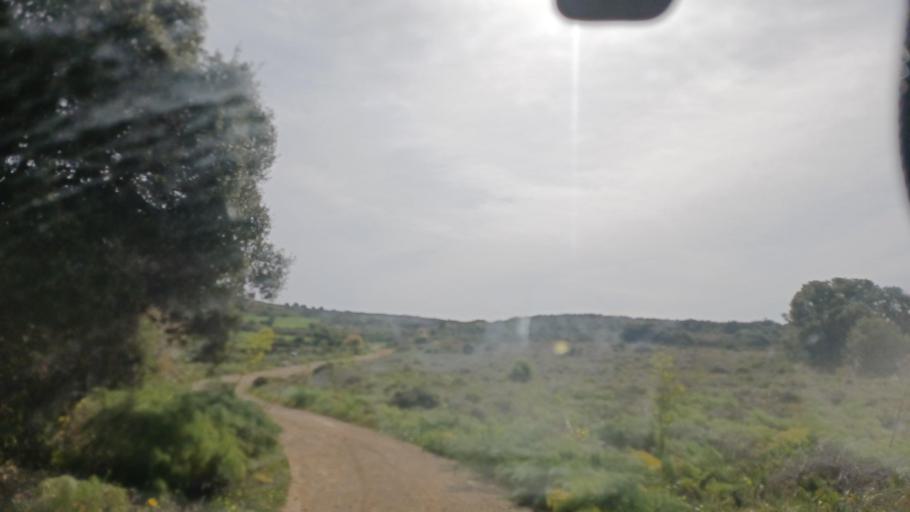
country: CY
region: Pafos
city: Mesogi
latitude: 34.7823
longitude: 32.4695
